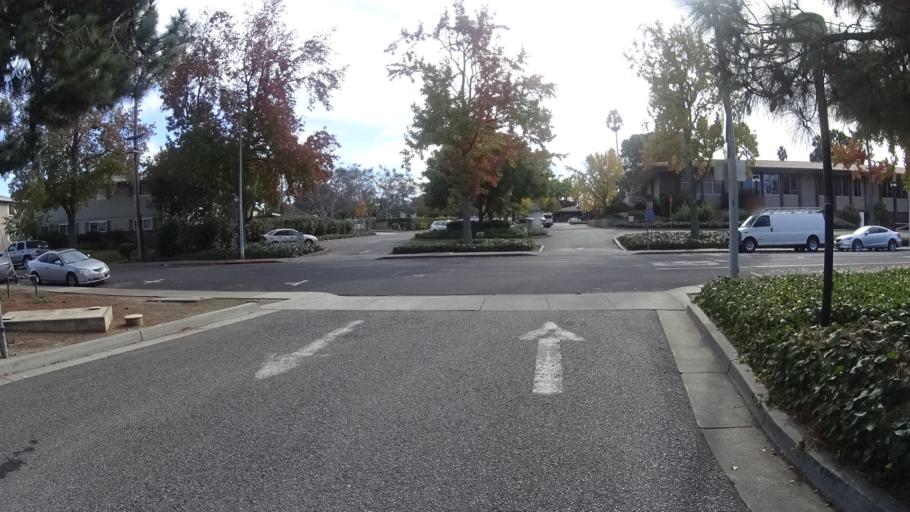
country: US
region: California
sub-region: Santa Clara County
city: Santa Clara
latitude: 37.3556
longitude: -121.9538
